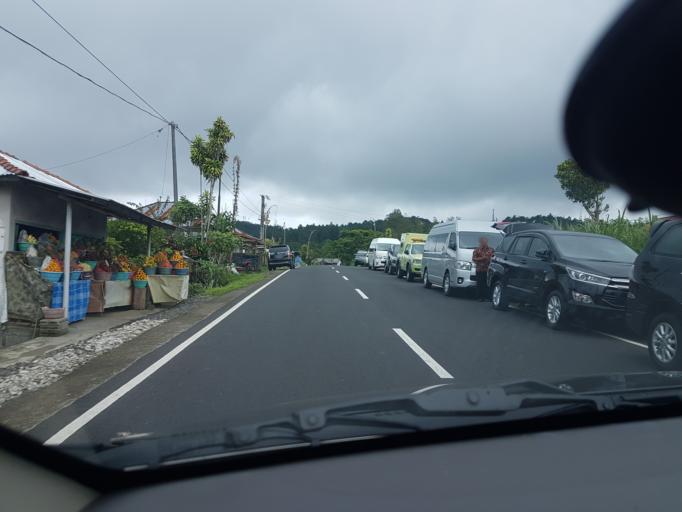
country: ID
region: Bali
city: Banjar Kedisan
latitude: -8.2942
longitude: 115.3584
